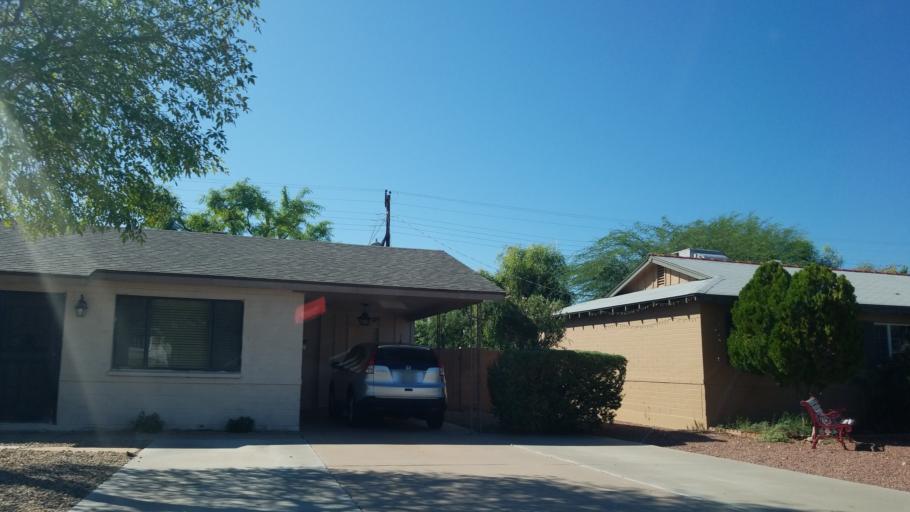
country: US
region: Arizona
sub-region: Maricopa County
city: Tempe
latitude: 33.4585
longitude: -111.9193
